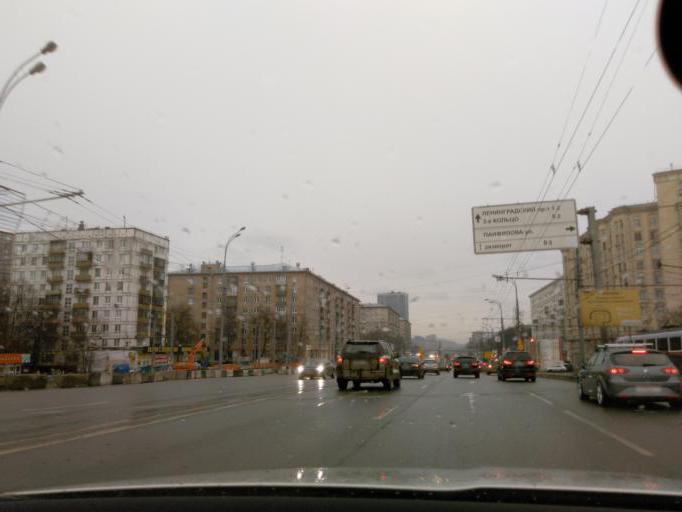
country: RU
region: Moskovskaya
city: Koptevo
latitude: 55.8098
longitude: 37.4904
